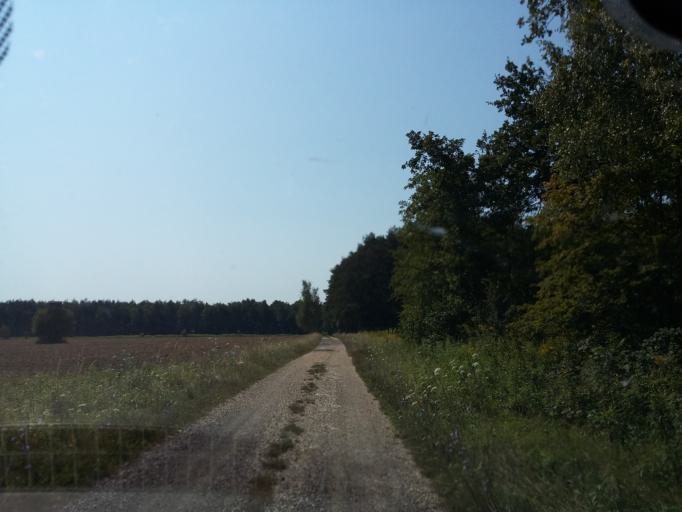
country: SI
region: Hodos-Hodos
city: Hodos
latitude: 46.8484
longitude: 16.3203
